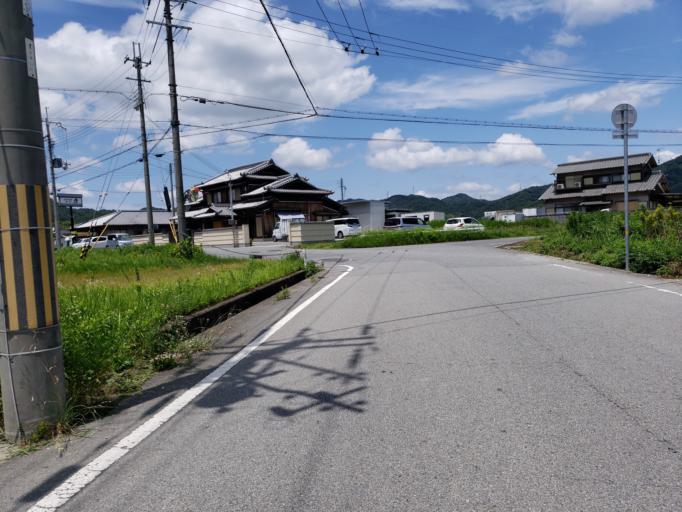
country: JP
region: Hyogo
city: Kakogawacho-honmachi
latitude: 34.8138
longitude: 134.8130
